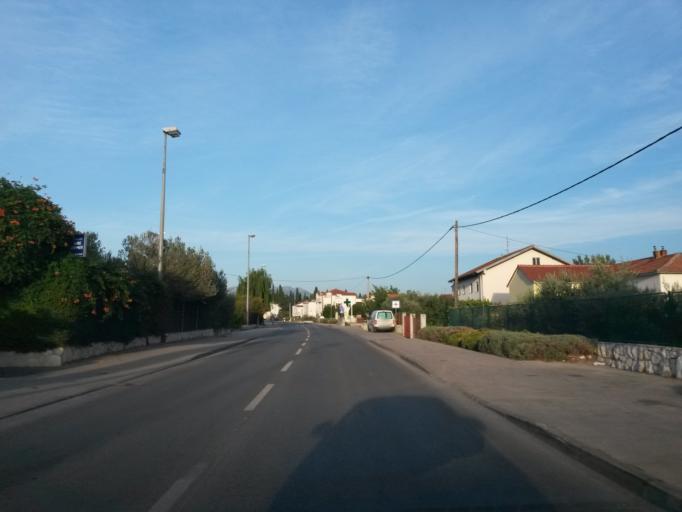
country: HR
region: Splitsko-Dalmatinska
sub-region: Grad Split
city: Split
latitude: 43.5536
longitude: 16.3494
